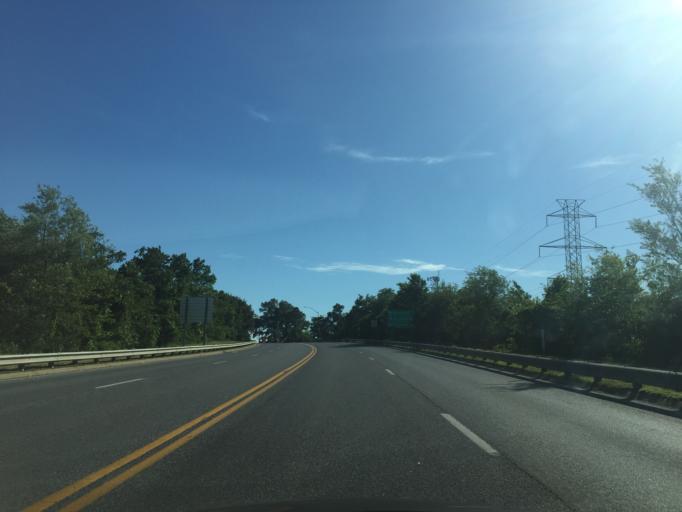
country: US
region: Maryland
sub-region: Baltimore County
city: Reisterstown
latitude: 39.4750
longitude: -76.8343
